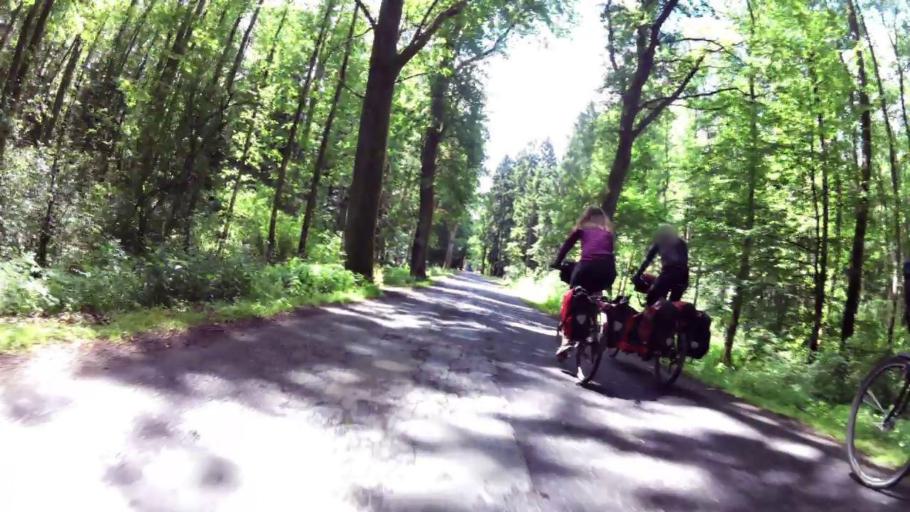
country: PL
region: West Pomeranian Voivodeship
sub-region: Powiat lobeski
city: Resko
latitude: 53.7547
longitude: 15.5103
